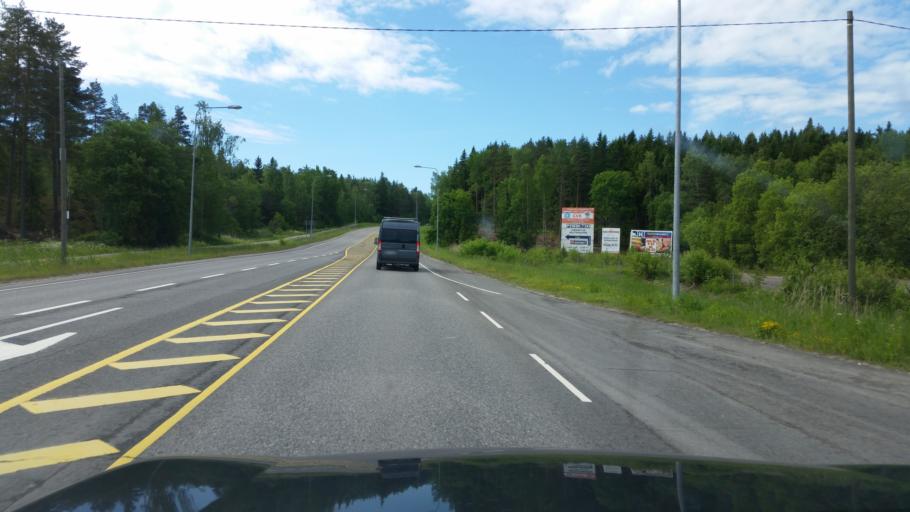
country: FI
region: Varsinais-Suomi
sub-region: Aboland-Turunmaa
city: Pargas
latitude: 60.3197
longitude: 22.3385
